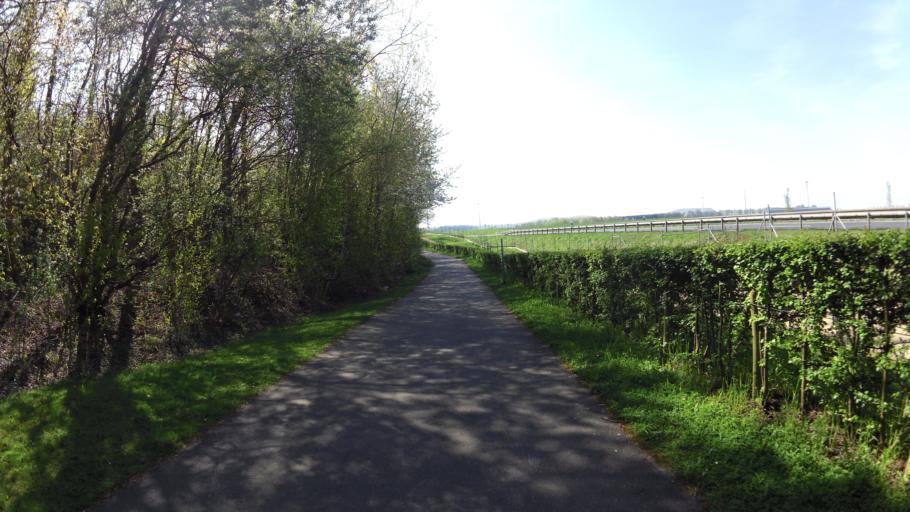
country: DE
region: North Rhine-Westphalia
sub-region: Regierungsbezirk Koln
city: Alsdorf
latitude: 50.9084
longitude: 6.1514
